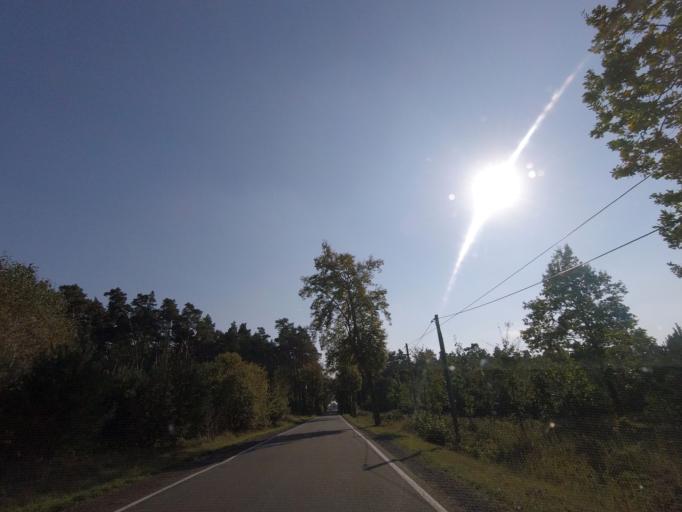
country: DE
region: Saxony-Anhalt
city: Jessen
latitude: 51.8619
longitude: 13.0254
